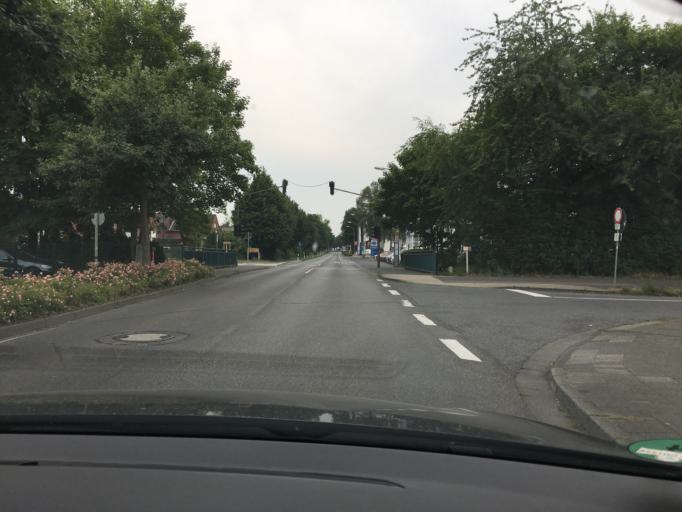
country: DE
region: North Rhine-Westphalia
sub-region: Regierungsbezirk Koln
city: Kerpen
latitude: 50.8793
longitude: 6.6943
